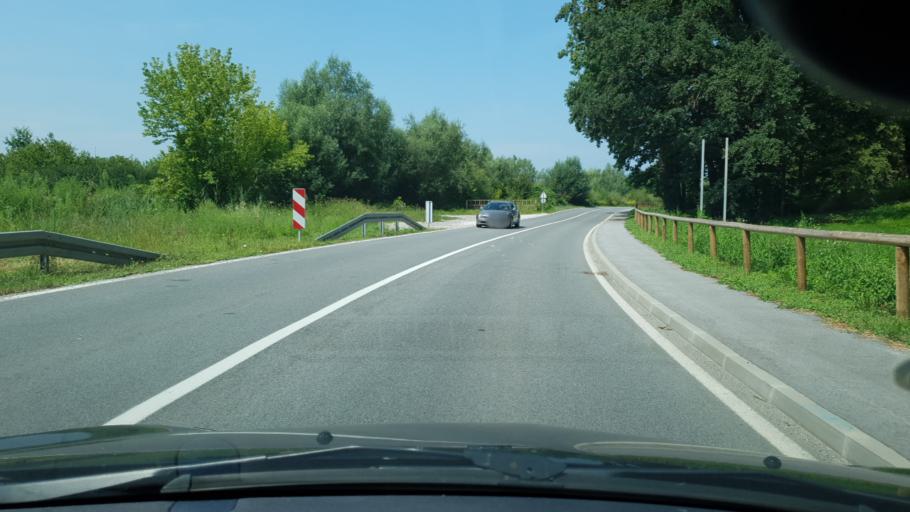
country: HR
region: Krapinsko-Zagorska
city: Zabok
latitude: 46.0159
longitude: 15.9381
